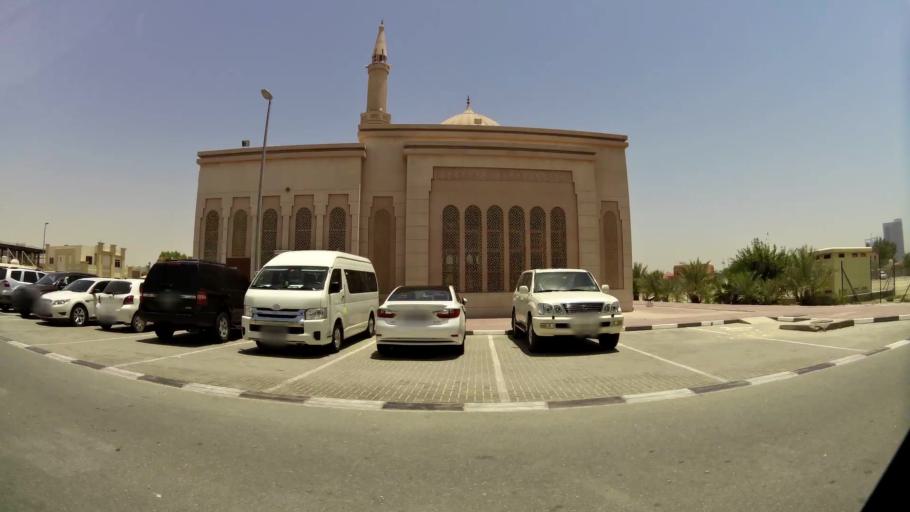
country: AE
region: Dubai
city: Dubai
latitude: 25.1048
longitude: 55.1921
